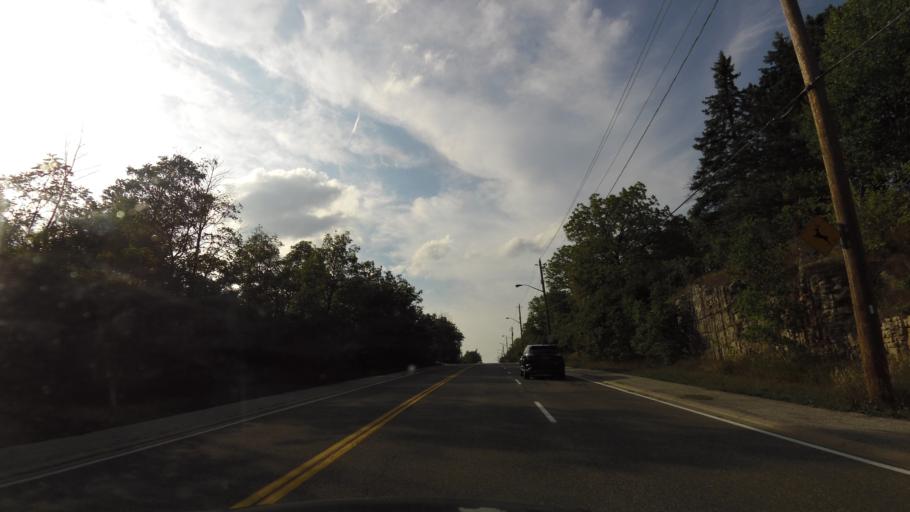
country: CA
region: Ontario
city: Burlington
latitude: 43.3660
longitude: -79.8592
